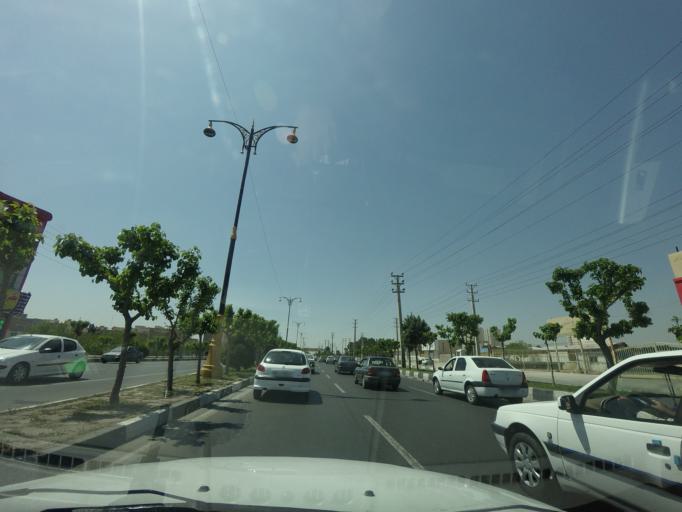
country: IR
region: Tehran
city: Eslamshahr
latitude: 35.5435
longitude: 51.2164
